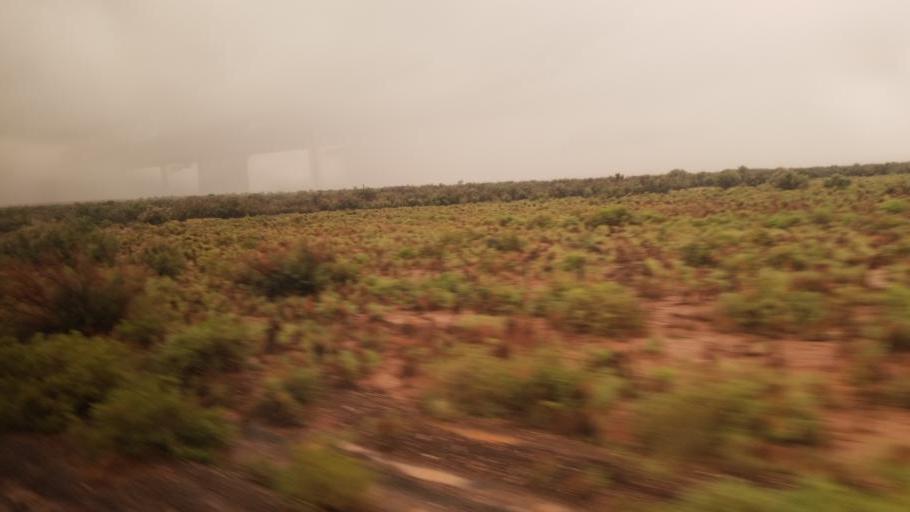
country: US
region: Arizona
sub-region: Navajo County
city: Joseph City
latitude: 34.9674
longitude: -110.4650
